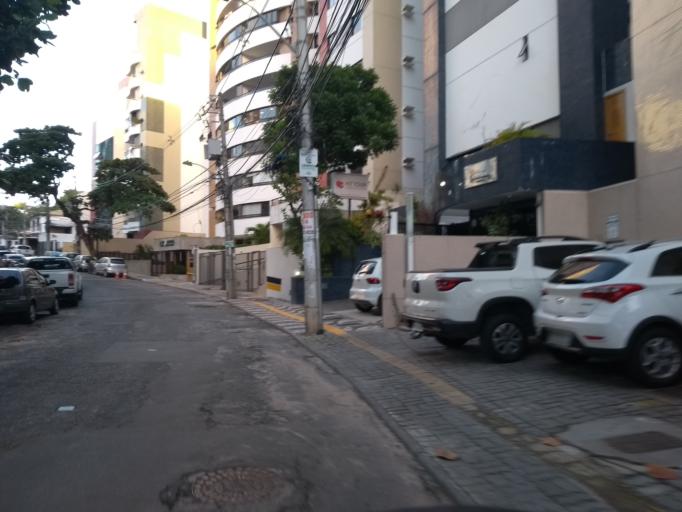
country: BR
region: Bahia
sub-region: Salvador
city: Salvador
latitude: -12.9977
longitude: -38.4611
